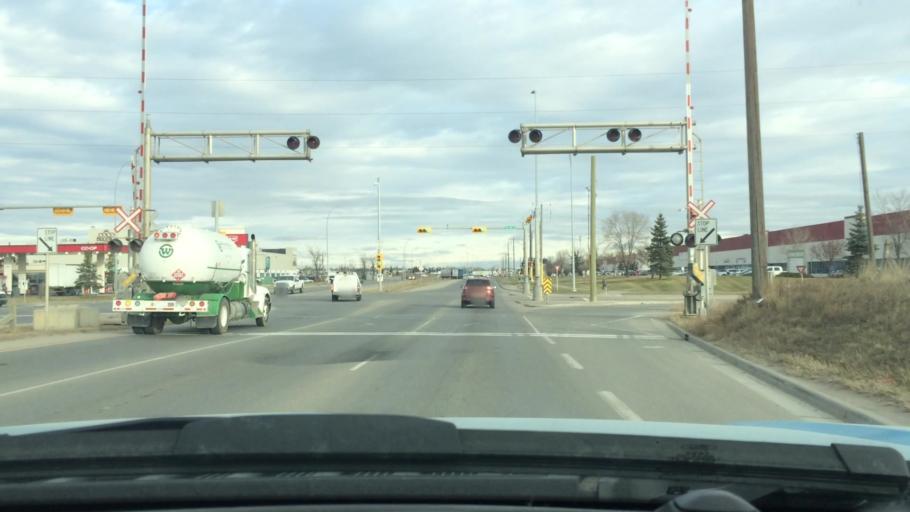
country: CA
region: Alberta
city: Calgary
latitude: 51.0082
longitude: -113.9583
